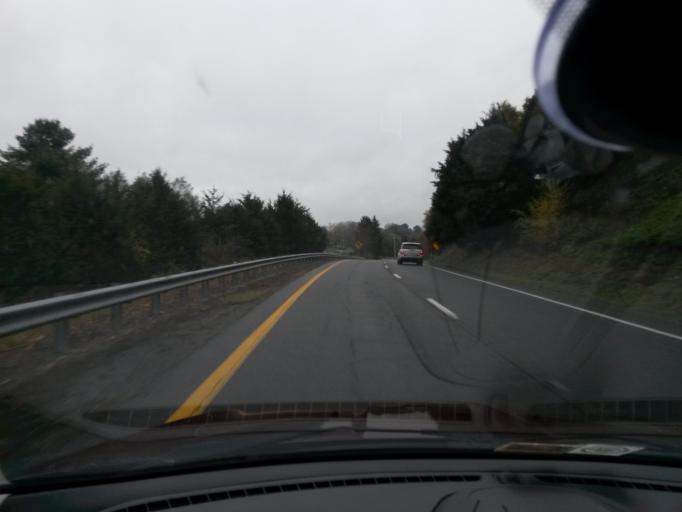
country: US
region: Virginia
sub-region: Botetourt County
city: Fincastle
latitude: 37.4885
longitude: -79.8782
